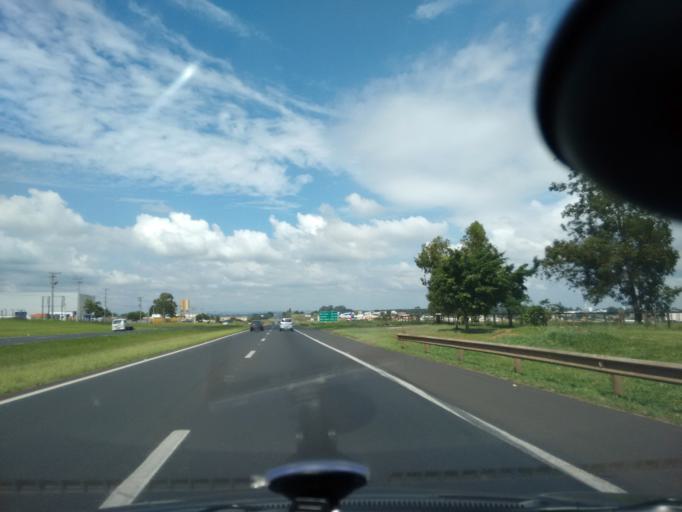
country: BR
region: Sao Paulo
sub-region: Sao Carlos
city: Sao Carlos
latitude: -22.0234
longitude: -47.8587
